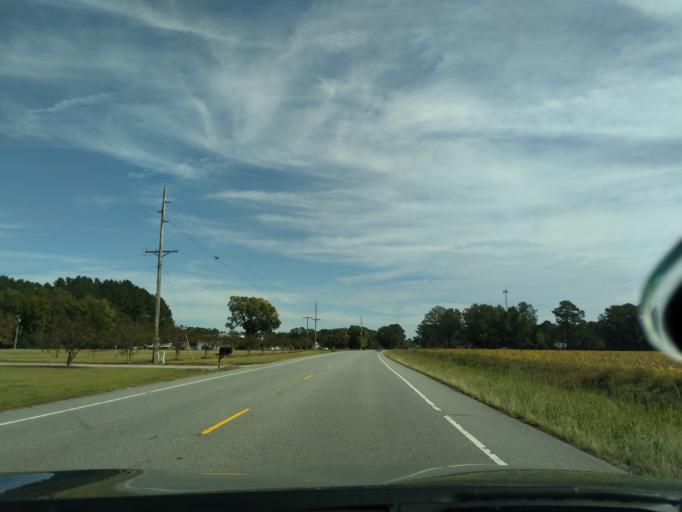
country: US
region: North Carolina
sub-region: Beaufort County
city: River Road
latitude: 35.5168
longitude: -76.9193
